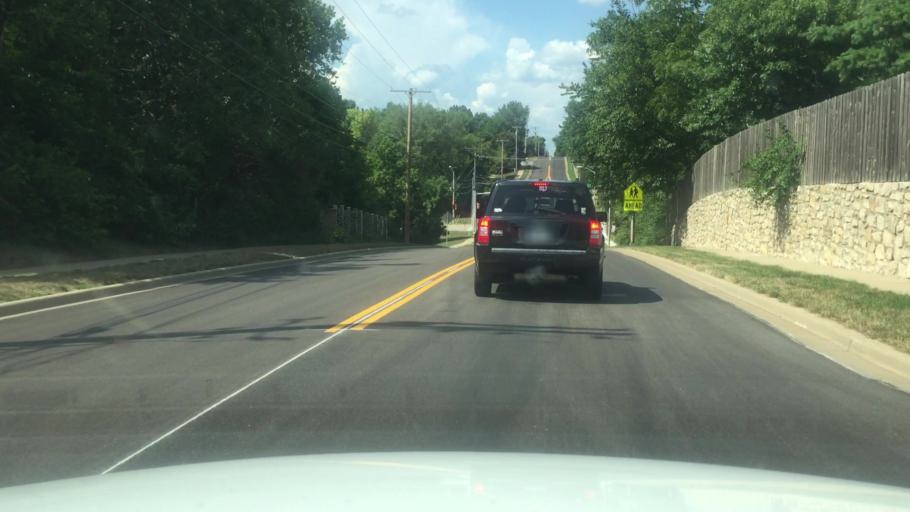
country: US
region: Kansas
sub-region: Johnson County
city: Lenexa
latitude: 38.9770
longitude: -94.7423
